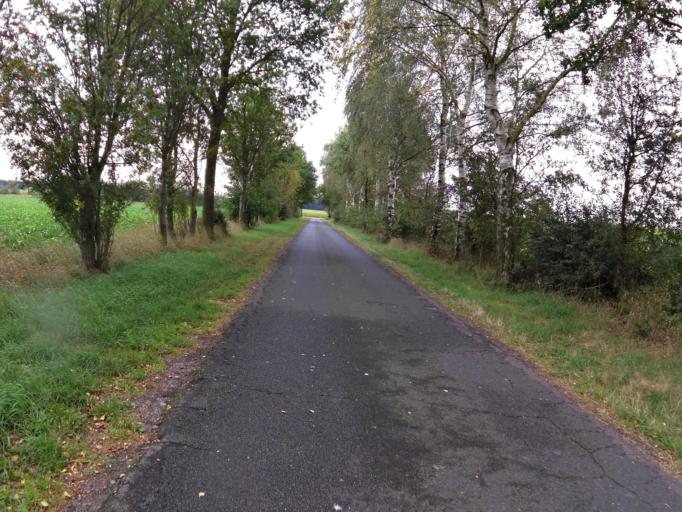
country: DE
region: Lower Saxony
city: Scheessel
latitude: 53.1899
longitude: 9.4700
